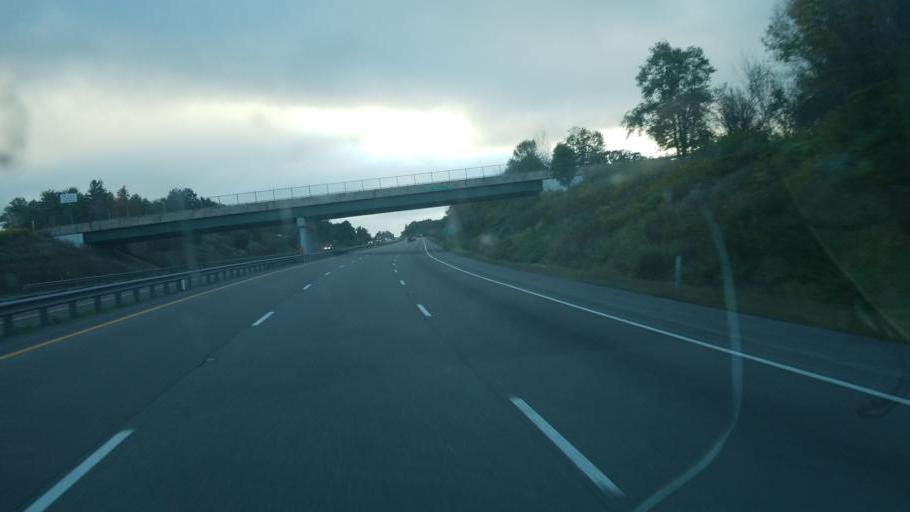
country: US
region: Pennsylvania
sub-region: Somerset County
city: Meyersdale
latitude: 39.6944
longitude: -79.1209
